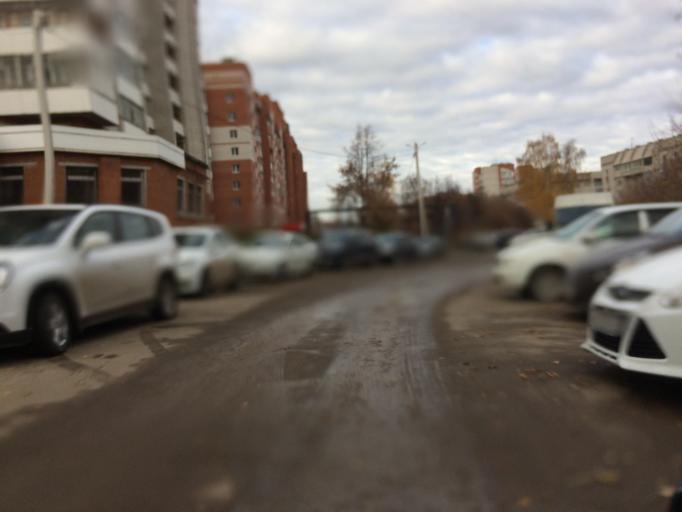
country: RU
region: Mariy-El
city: Yoshkar-Ola
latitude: 56.6415
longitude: 47.8646
